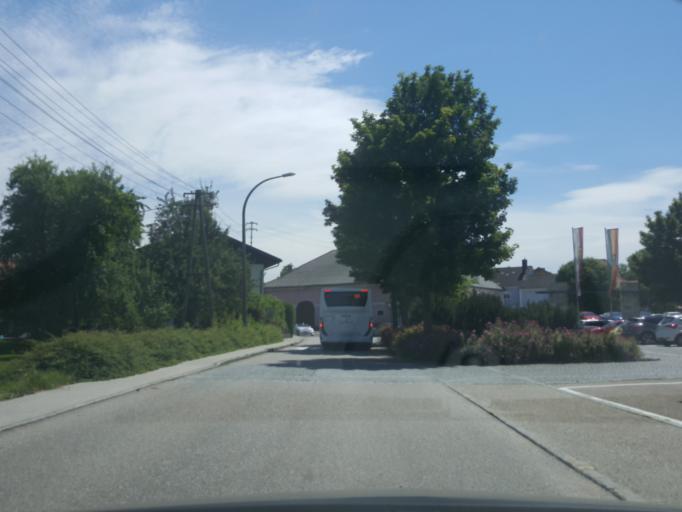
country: AT
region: Upper Austria
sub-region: Politischer Bezirk Vocklabruck
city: Seewalchen
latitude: 47.9547
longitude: 13.5855
